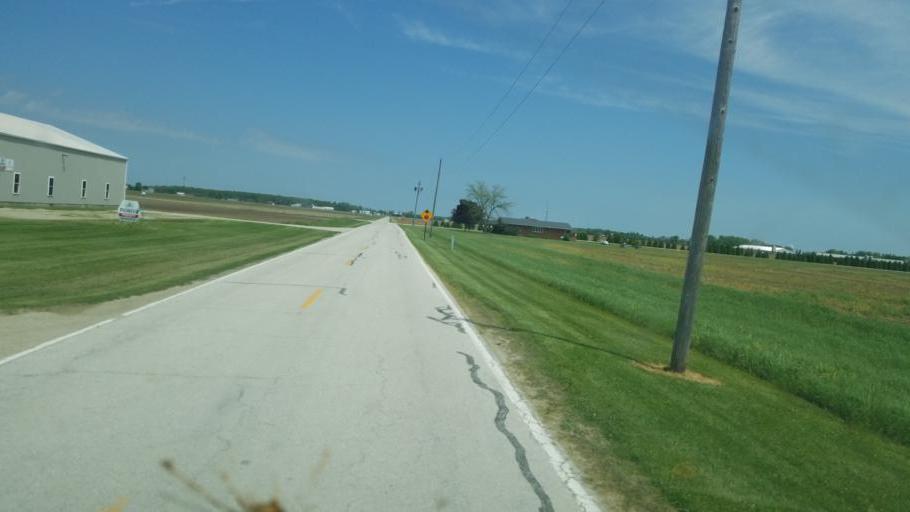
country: US
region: Ohio
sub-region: Ottawa County
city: Oak Harbor
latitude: 41.4564
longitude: -83.2017
